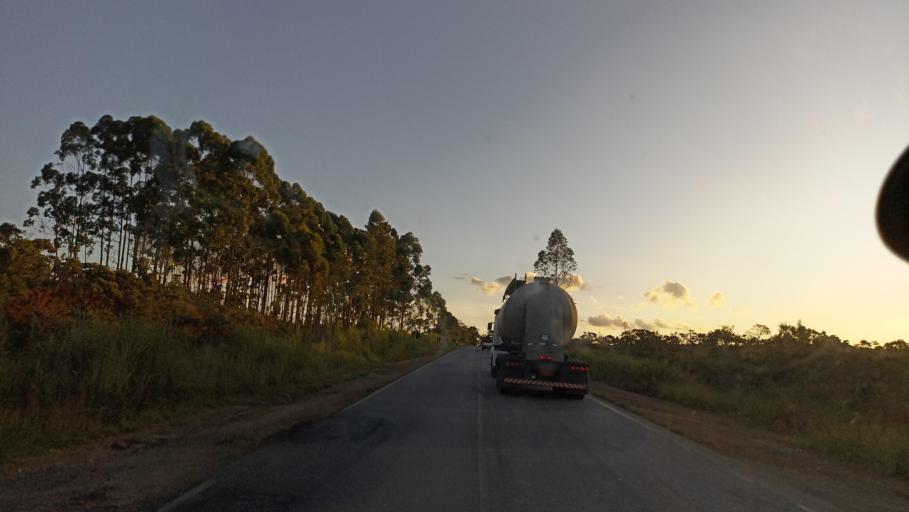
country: BR
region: Minas Gerais
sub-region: Sao Joao Del Rei
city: Sao Joao del Rei
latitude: -21.2367
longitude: -44.3959
